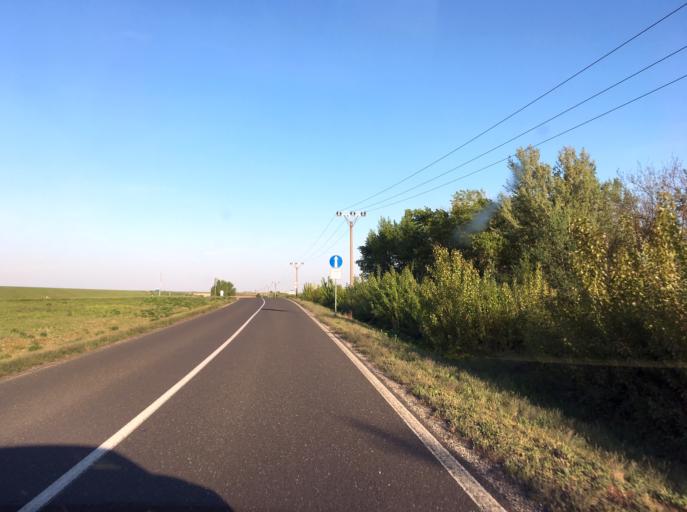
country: SK
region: Trnavsky
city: Samorin
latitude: 47.9947
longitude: 17.3374
